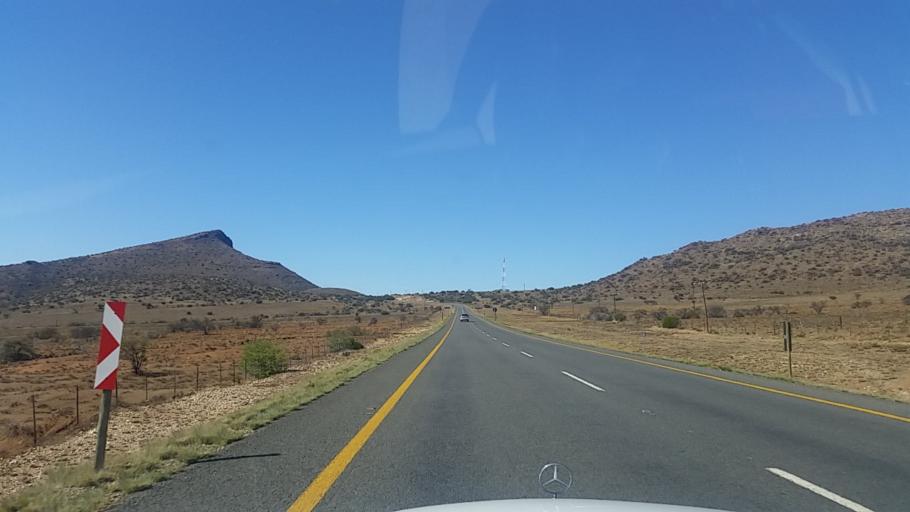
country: ZA
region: Eastern Cape
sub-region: Cacadu District Municipality
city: Graaff-Reinet
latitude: -32.0997
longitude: 24.6052
